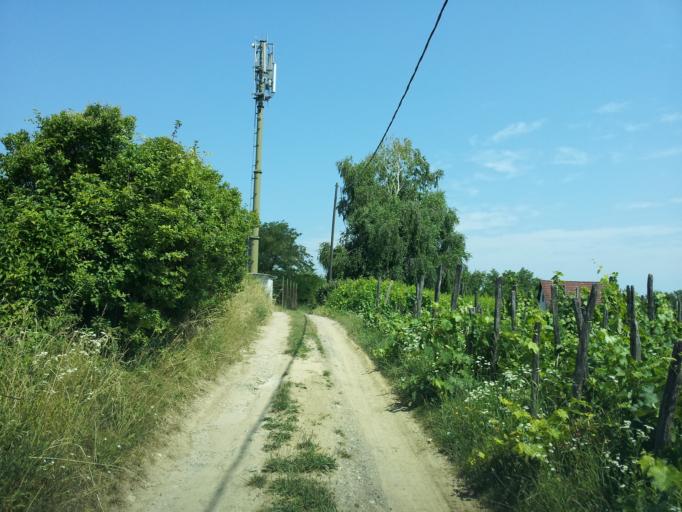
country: HU
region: Zala
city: Pacsa
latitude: 46.8260
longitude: 16.9686
